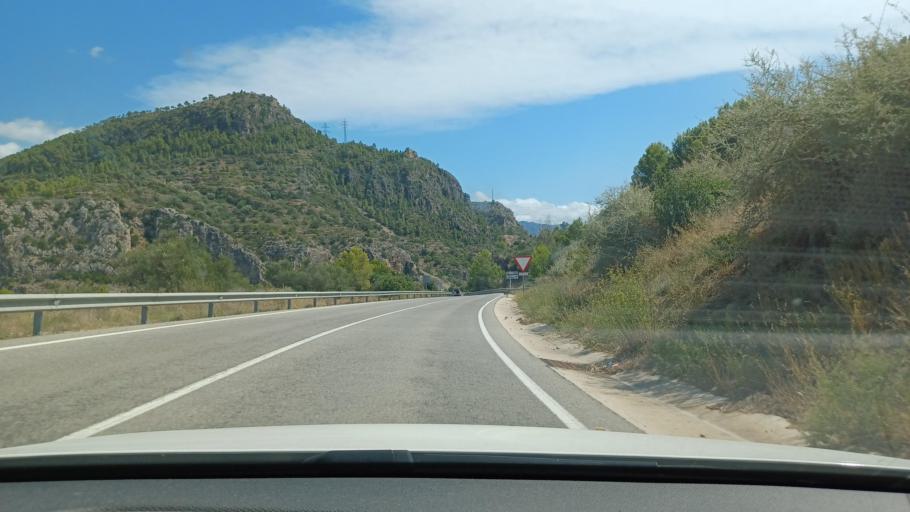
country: ES
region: Catalonia
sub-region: Provincia de Tarragona
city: Tivenys
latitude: 40.9332
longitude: 0.4827
